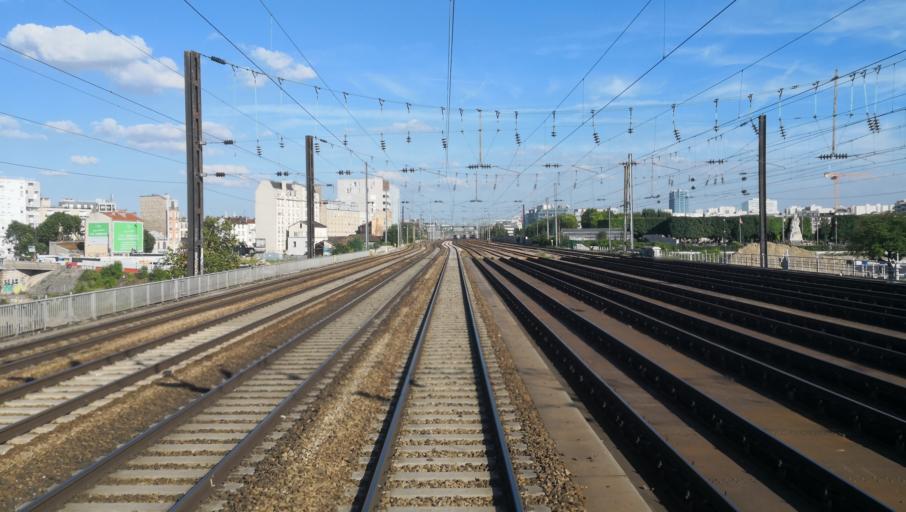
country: FR
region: Ile-de-France
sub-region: Departement des Hauts-de-Seine
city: Levallois-Perret
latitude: 48.9038
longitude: 2.2872
